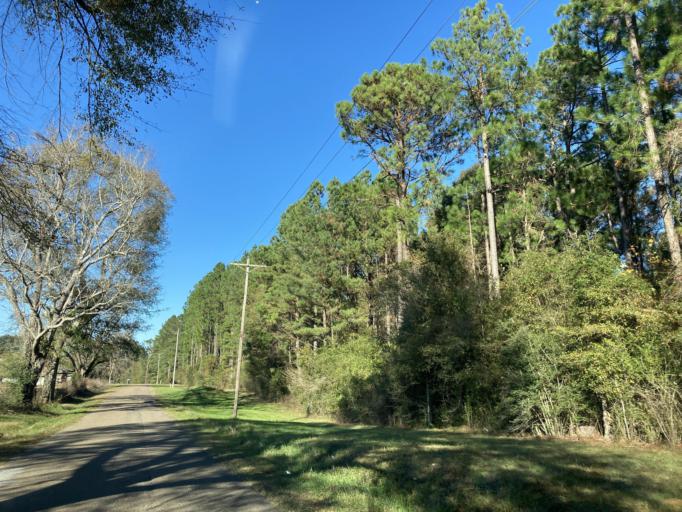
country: US
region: Mississippi
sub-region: Lamar County
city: Sumrall
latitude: 31.3546
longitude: -89.6030
